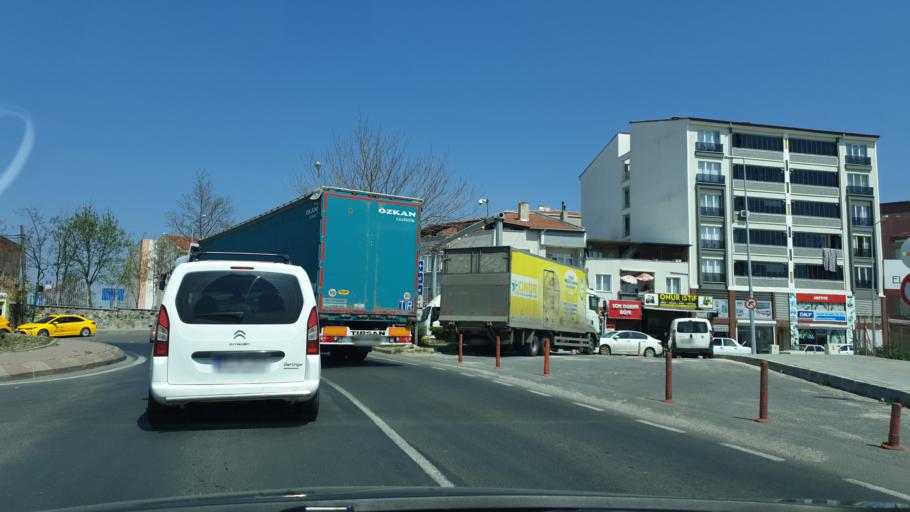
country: TR
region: Tekirdag
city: Corlu
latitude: 41.1632
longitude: 27.7879
